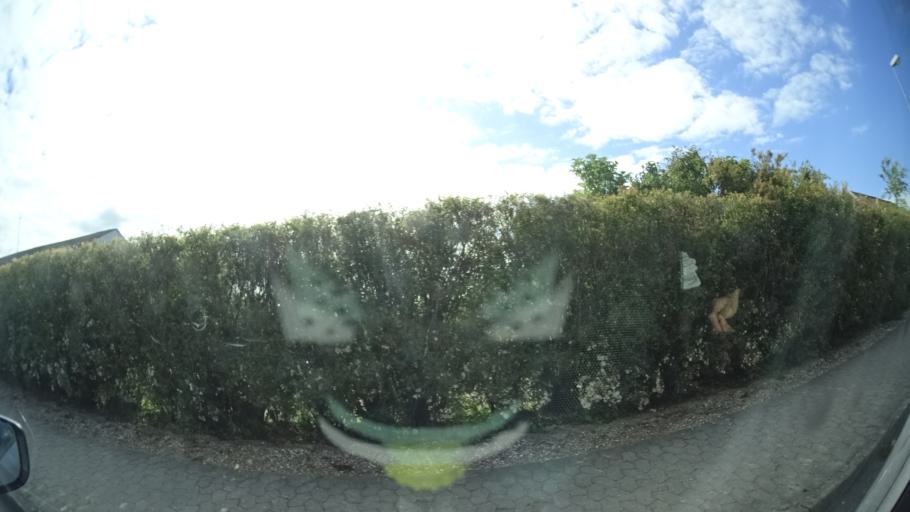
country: DK
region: Central Jutland
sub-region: Norddjurs Kommune
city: Grenaa
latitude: 56.5292
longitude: 10.7111
